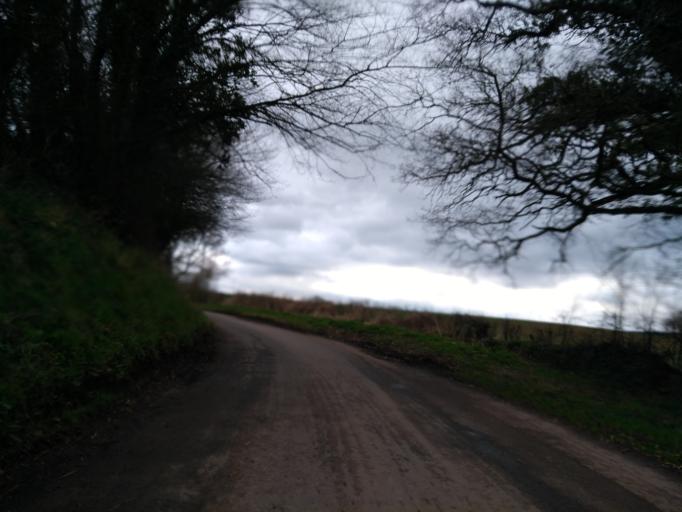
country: GB
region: England
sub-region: Devon
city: Crediton
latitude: 50.7844
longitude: -3.6069
